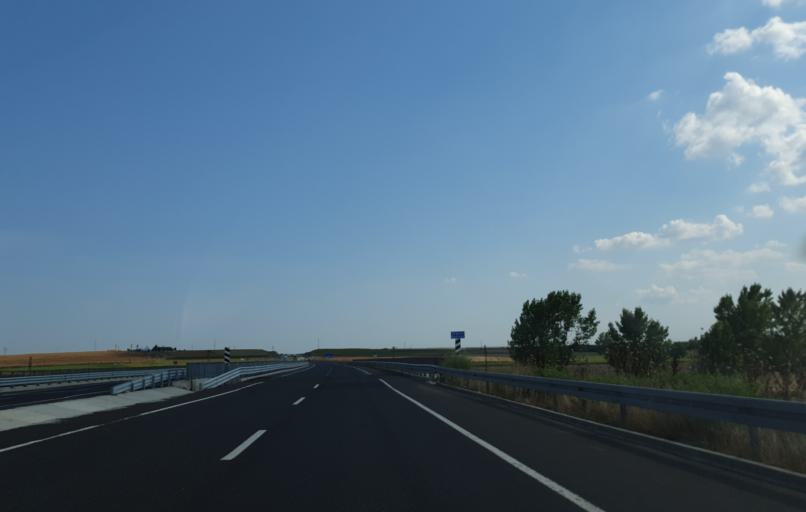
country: TR
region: Tekirdag
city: Muratli
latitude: 41.2191
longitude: 27.5324
